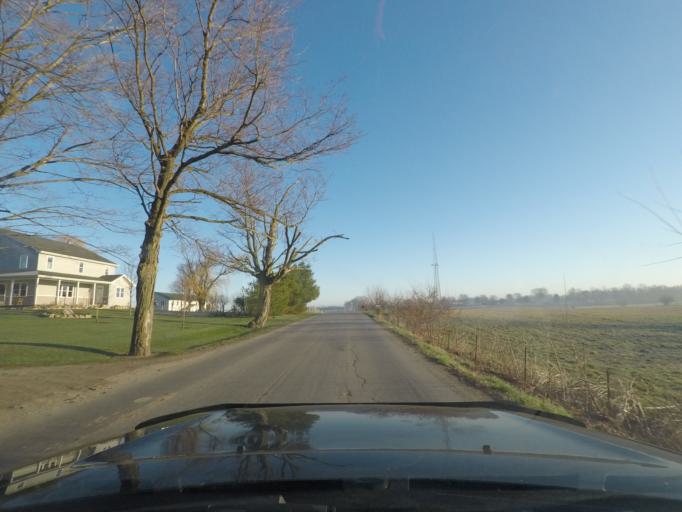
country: US
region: Indiana
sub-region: Elkhart County
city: Dunlap
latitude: 41.5463
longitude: -85.9247
